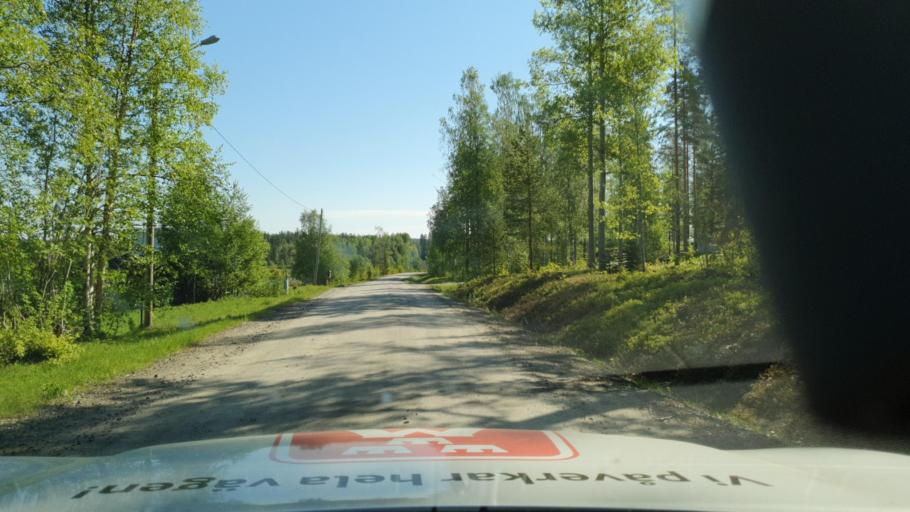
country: SE
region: Vaesterbotten
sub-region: Vannas Kommun
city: Vannasby
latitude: 63.9938
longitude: 19.7707
